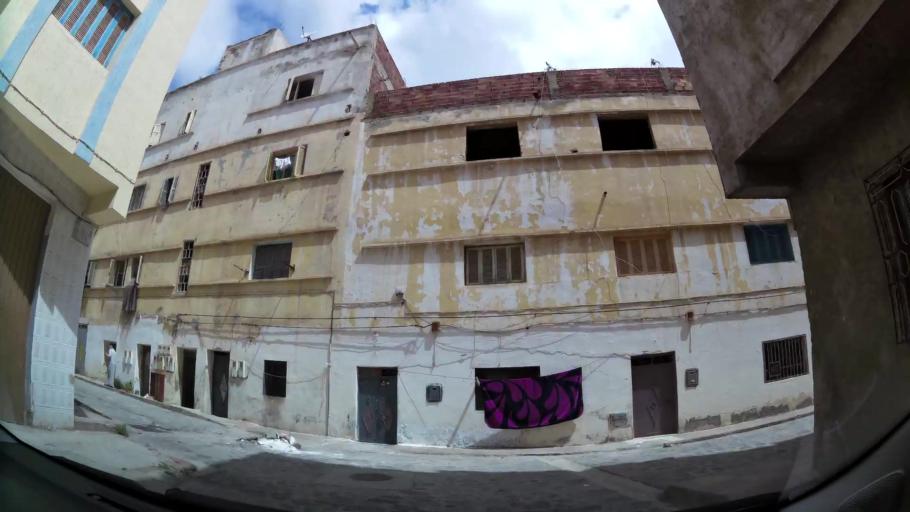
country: MA
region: Oriental
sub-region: Nador
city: Nador
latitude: 35.1635
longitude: -2.9263
